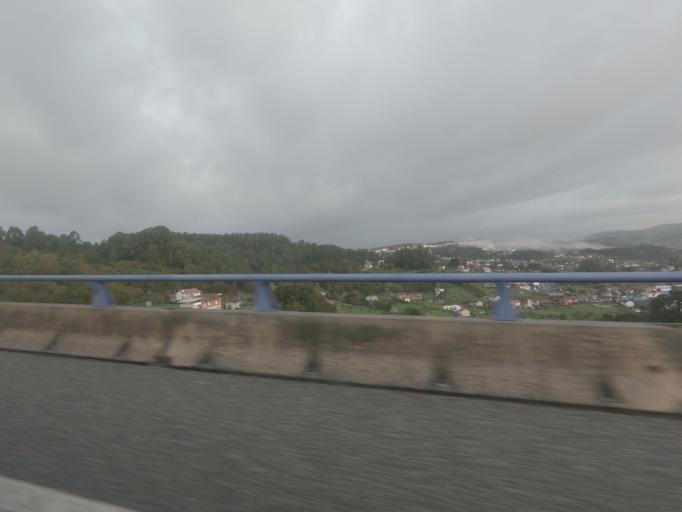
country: ES
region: Galicia
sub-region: Provincia de Pontevedra
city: Porrino
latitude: 42.1895
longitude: -8.6577
